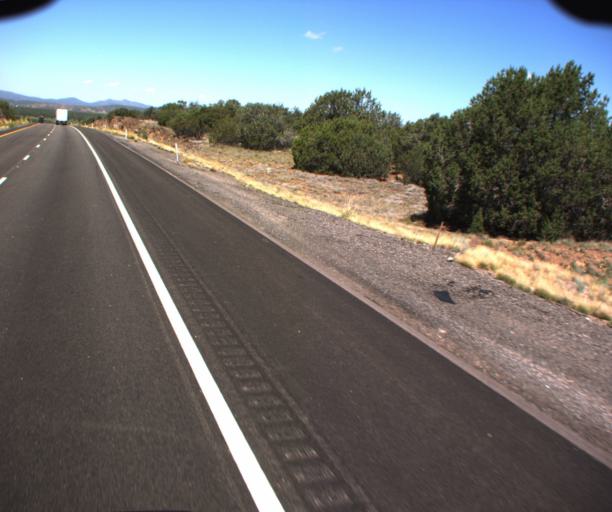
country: US
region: Arizona
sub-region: Mohave County
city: Peach Springs
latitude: 35.1909
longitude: -113.3288
